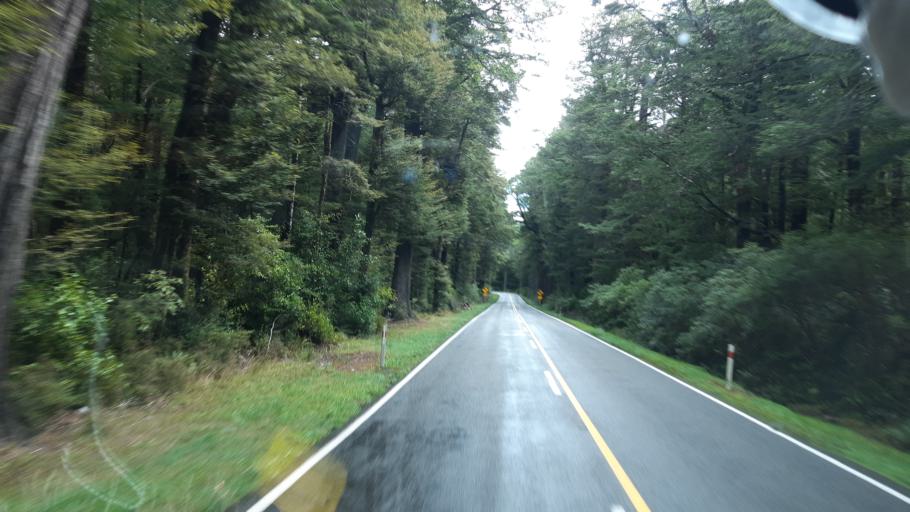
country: NZ
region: Canterbury
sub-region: Hurunui District
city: Amberley
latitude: -42.3807
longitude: 172.3087
